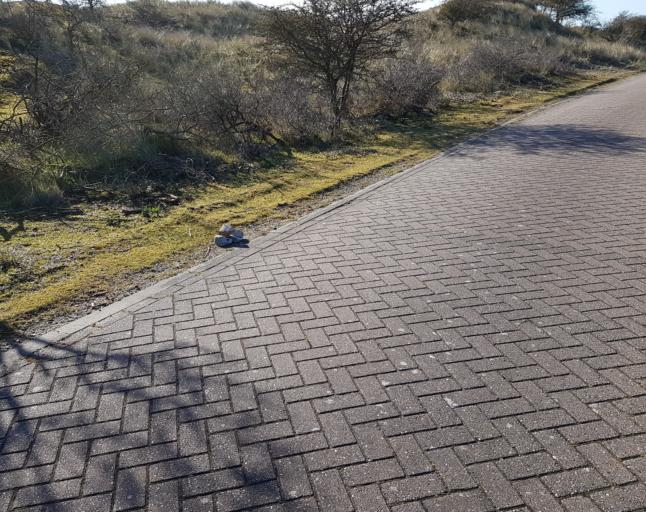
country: NL
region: North Holland
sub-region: Gemeente Zandvoort
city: Zandvoort
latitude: 52.3222
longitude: 4.5170
